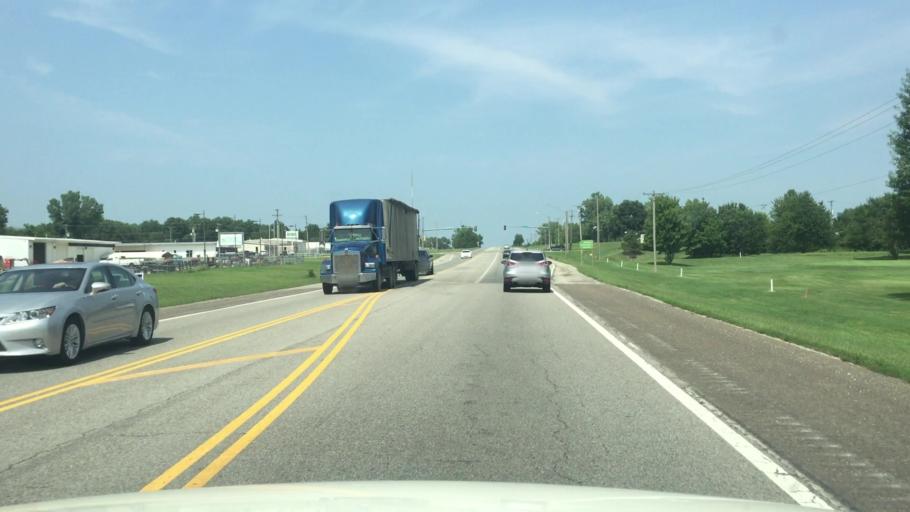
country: US
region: Kansas
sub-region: Crawford County
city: Pittsburg
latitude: 37.4237
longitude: -94.7173
